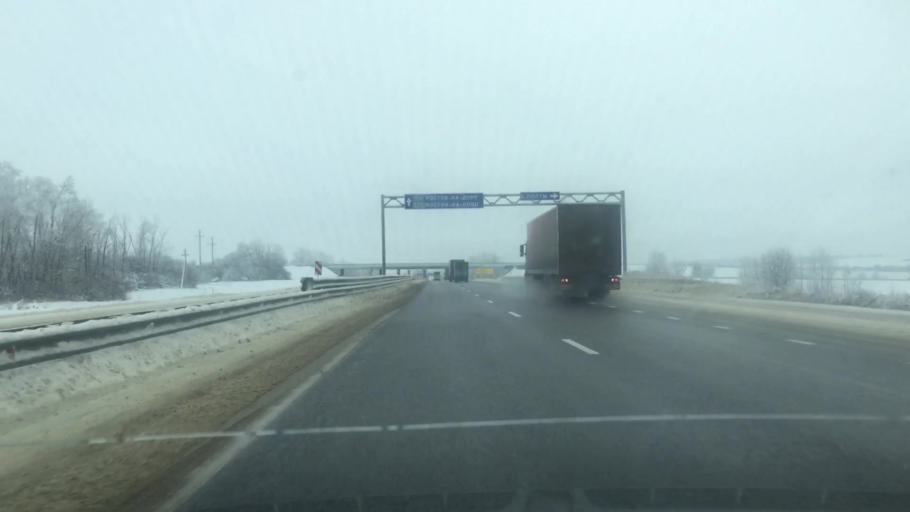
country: RU
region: Tula
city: Kazachka
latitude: 53.3027
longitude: 38.1782
